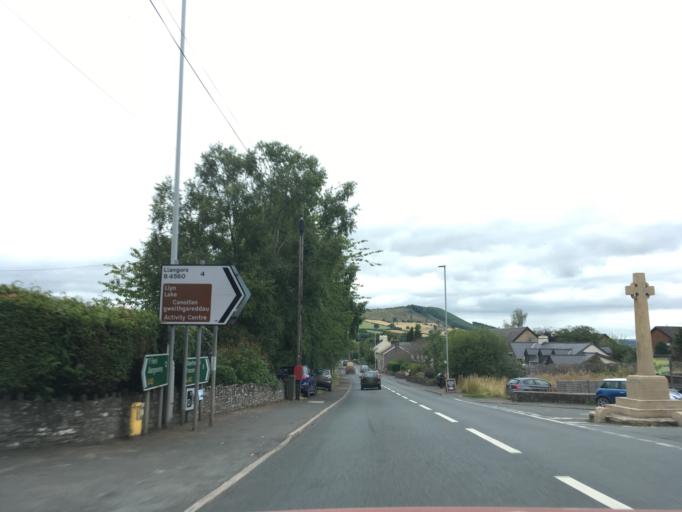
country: GB
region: Wales
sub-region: Blaenau Gwent
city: Brynmawr
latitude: 51.8925
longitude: -3.2419
